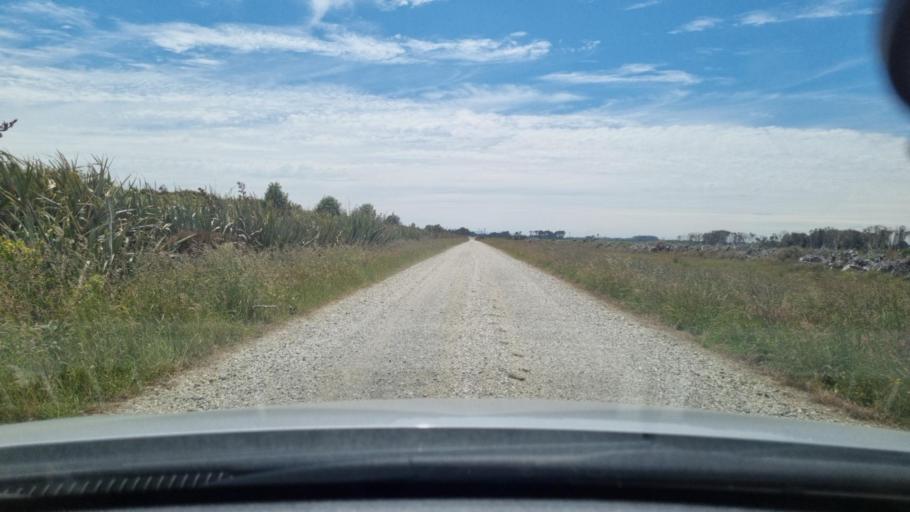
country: NZ
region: Southland
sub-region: Invercargill City
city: Invercargill
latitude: -46.3957
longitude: 168.2684
